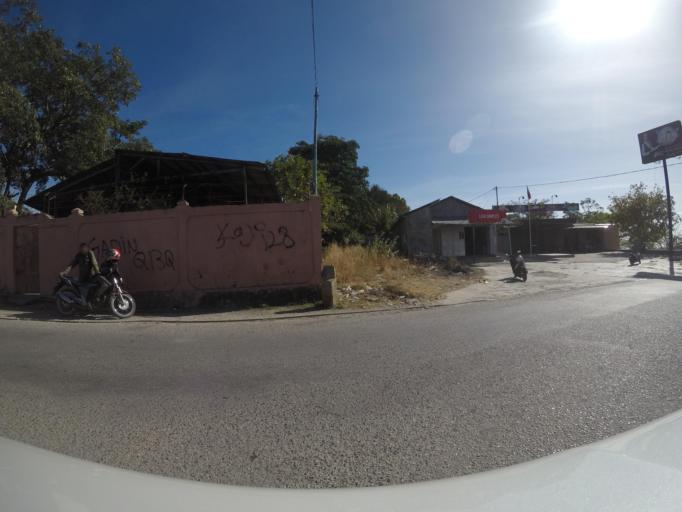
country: TL
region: Baucau
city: Baucau
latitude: -8.4625
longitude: 126.4588
